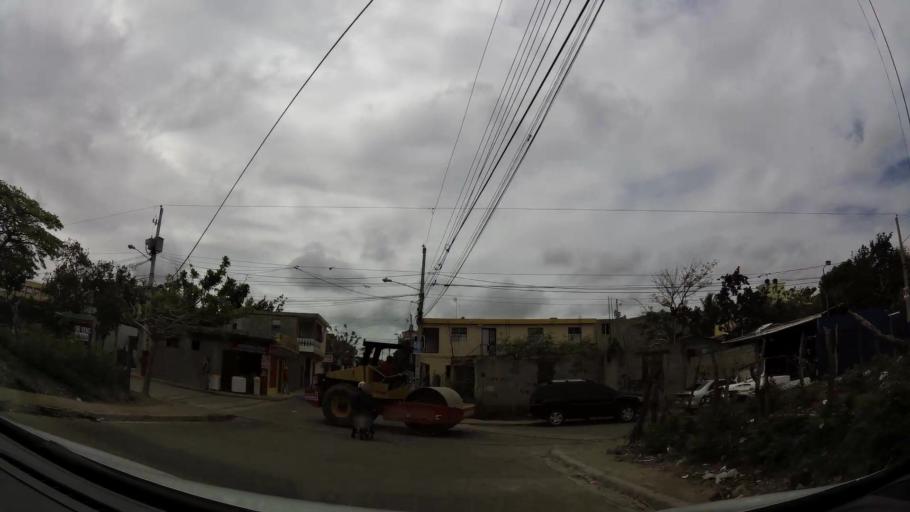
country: DO
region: Santiago
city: Santiago de los Caballeros
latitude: 19.4287
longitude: -70.6627
